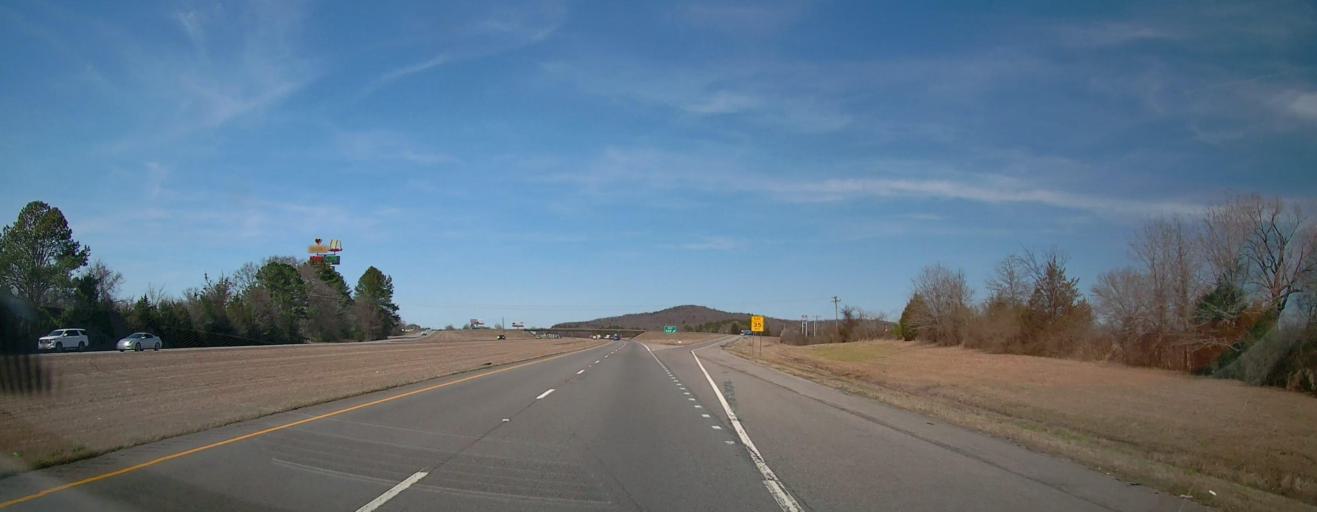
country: US
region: Alabama
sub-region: Morgan County
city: Falkville
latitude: 34.3630
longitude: -86.8912
